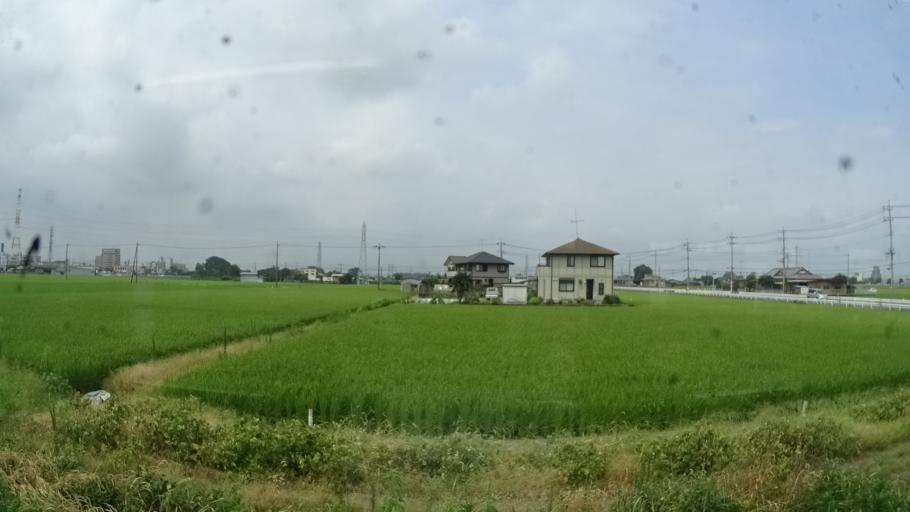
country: JP
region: Ibaraki
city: Shimodate
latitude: 36.3135
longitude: 139.9721
